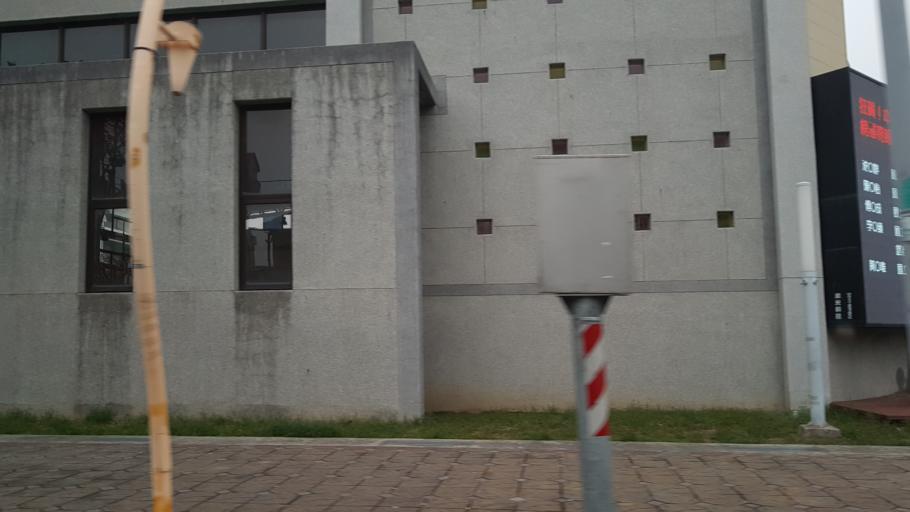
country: TW
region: Taiwan
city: Xinying
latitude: 23.3103
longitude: 120.3118
